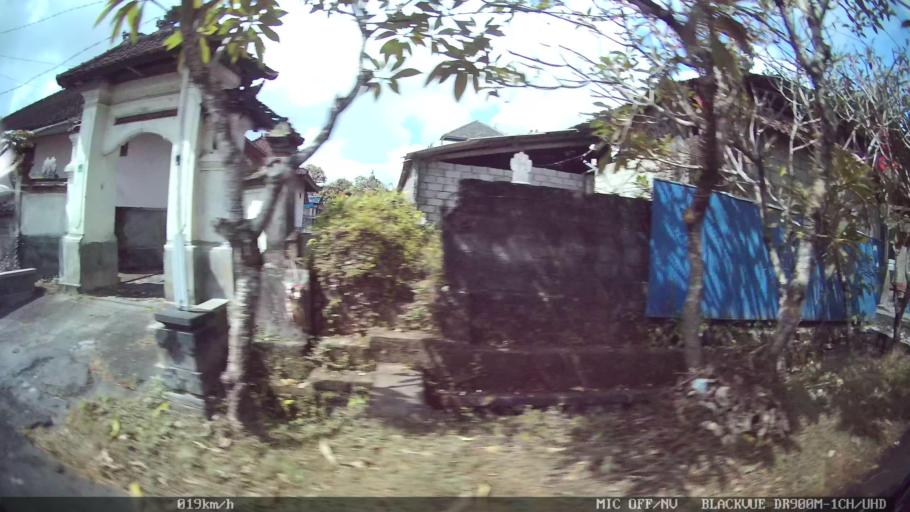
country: ID
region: Bali
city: Banjar Batur
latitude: -8.5978
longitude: 115.2088
